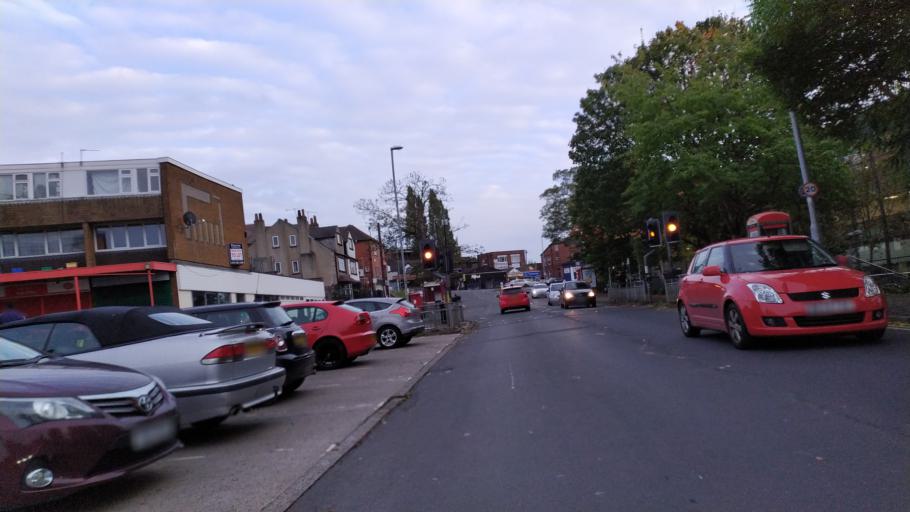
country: GB
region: England
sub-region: City and Borough of Leeds
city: Chapel Allerton
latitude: 53.8291
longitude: -1.5675
